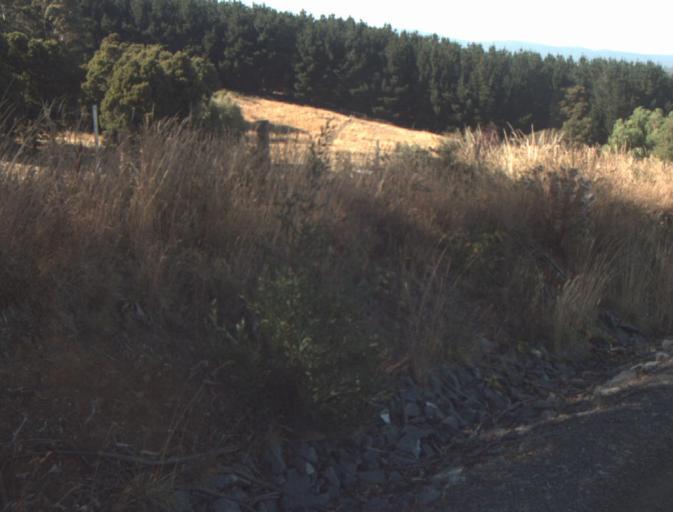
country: AU
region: Tasmania
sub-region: Dorset
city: Bridport
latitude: -41.1695
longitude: 147.2307
